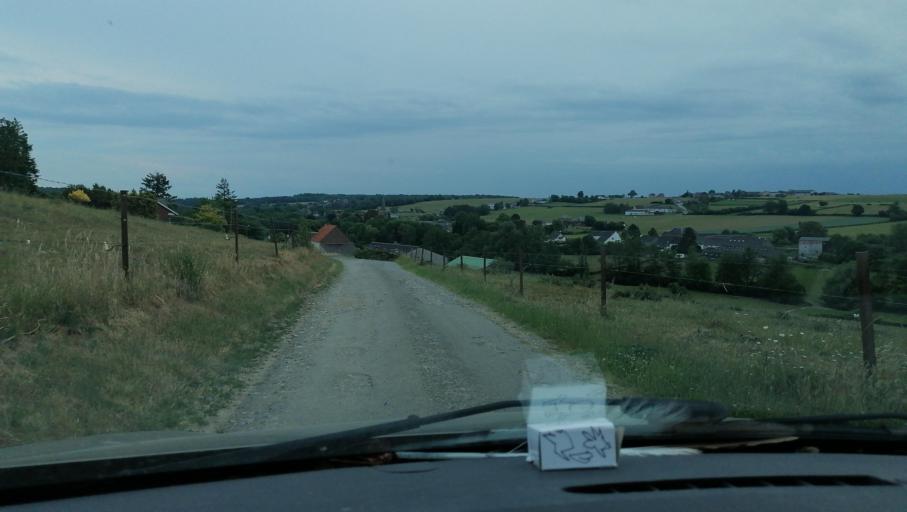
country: BE
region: Wallonia
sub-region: Province du Hainaut
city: Beaumont
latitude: 50.2043
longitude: 4.1650
